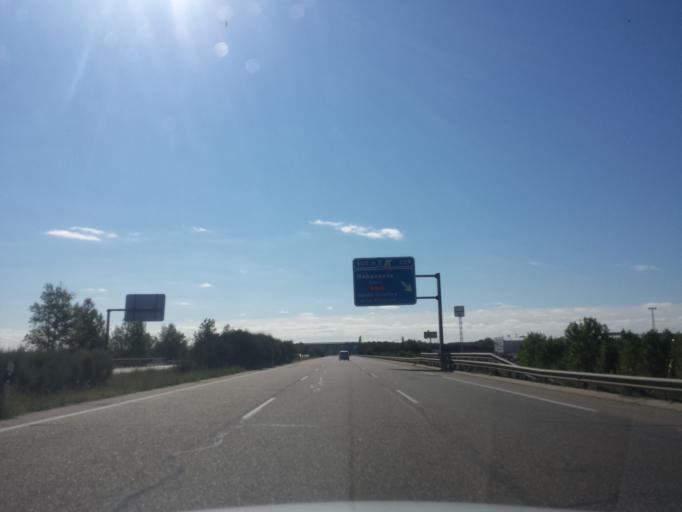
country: ES
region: Castille and Leon
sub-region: Provincia de Zamora
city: Villanueva de Azoague
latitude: 41.9949
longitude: -5.6469
